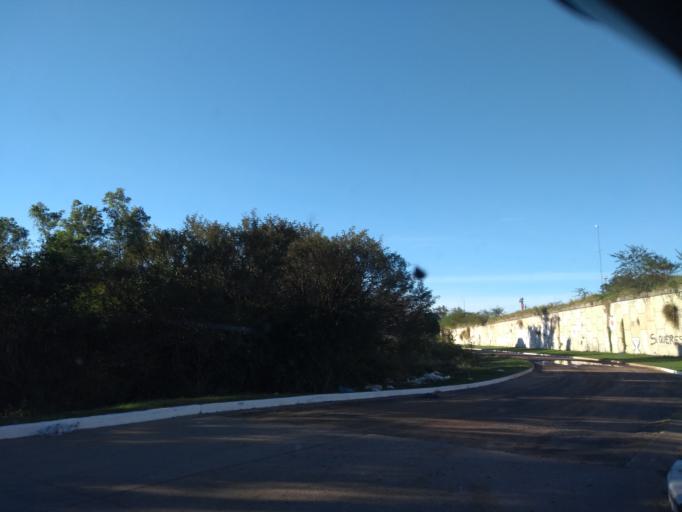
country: AR
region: Chaco
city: Barranqueras
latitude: -27.4906
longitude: -58.9272
